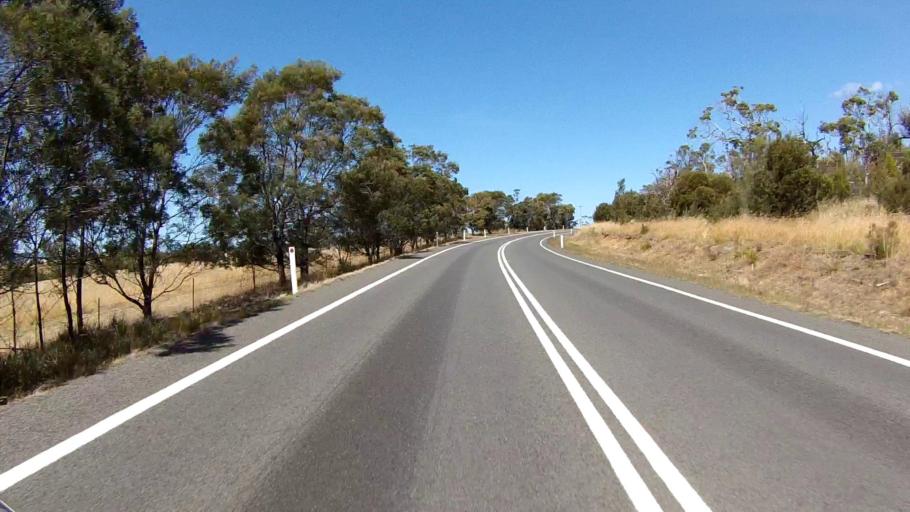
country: AU
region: Tasmania
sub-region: Break O'Day
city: St Helens
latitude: -42.0777
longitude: 148.0683
